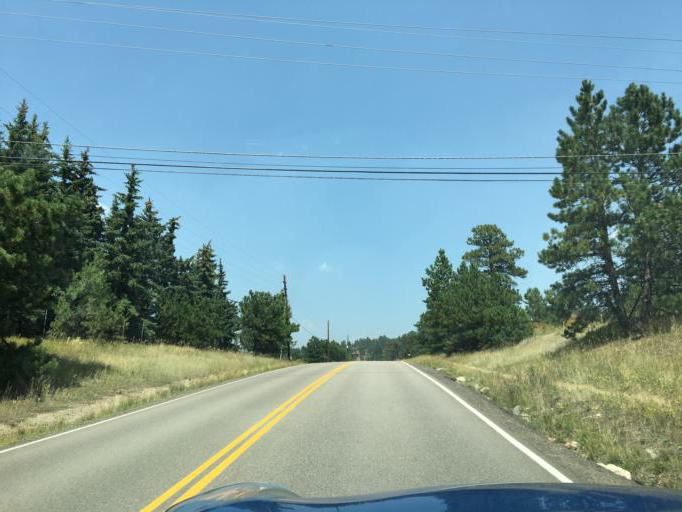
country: US
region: Colorado
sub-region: Jefferson County
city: Genesee
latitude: 39.7132
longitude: -105.2944
